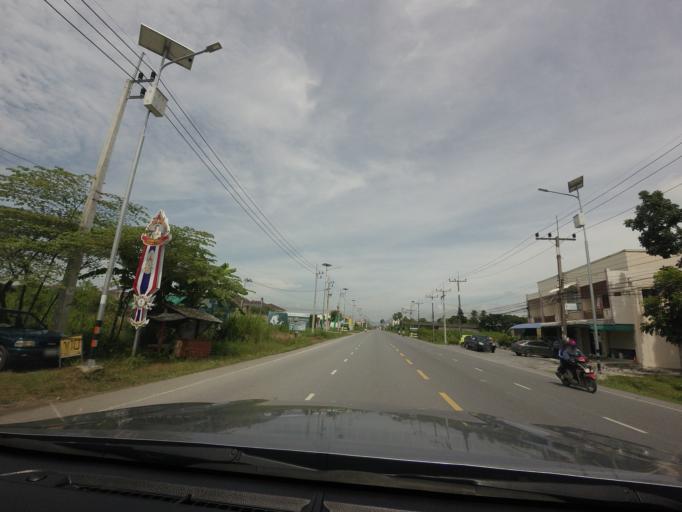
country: TH
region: Nakhon Si Thammarat
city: Nakhon Si Thammarat
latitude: 8.4456
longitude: 99.9907
